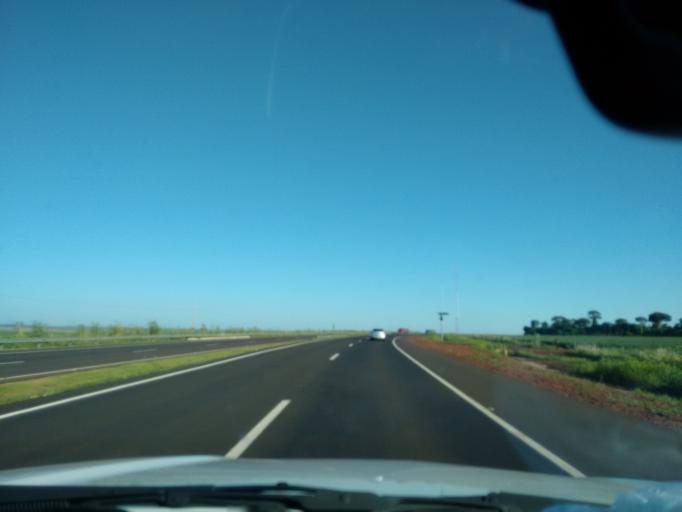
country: BR
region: Mato Grosso do Sul
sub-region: Caarapo
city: Caarapo
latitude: -22.7470
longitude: -54.7896
